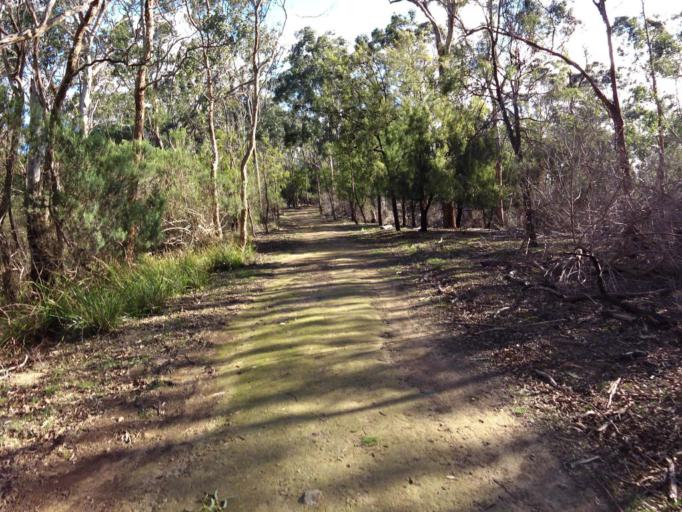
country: AU
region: Victoria
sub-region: Nillumbik
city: North Warrandyte
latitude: -37.7357
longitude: 145.2058
